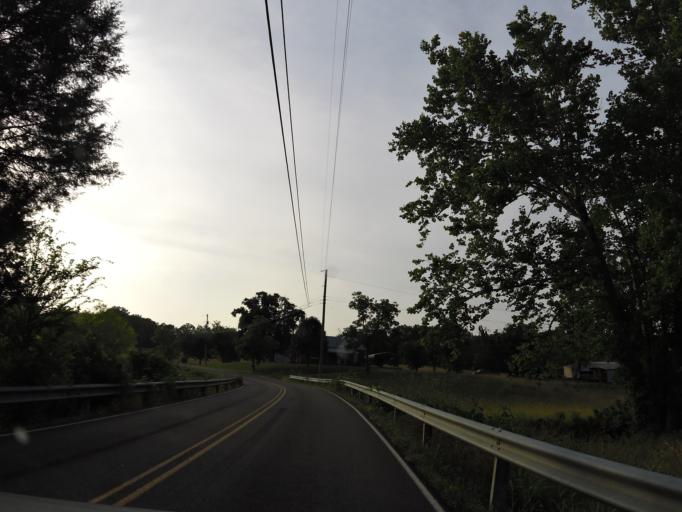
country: US
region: Tennessee
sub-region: Sevier County
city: Seymour
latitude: 35.9041
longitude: -83.8031
